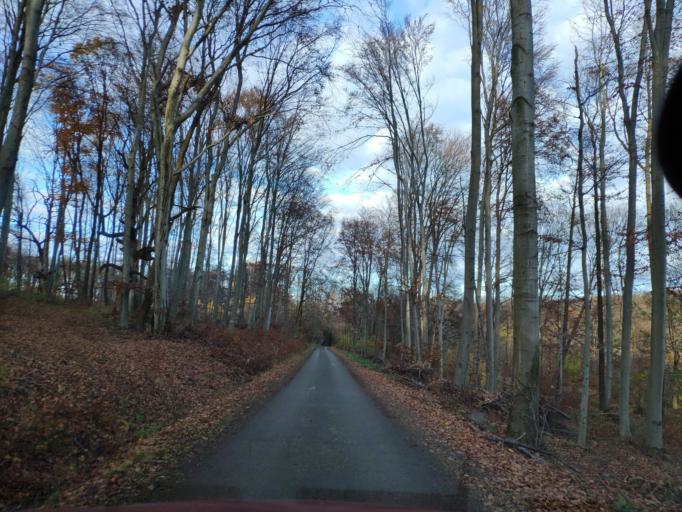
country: SK
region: Kosicky
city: Secovce
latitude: 48.5795
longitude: 21.4814
